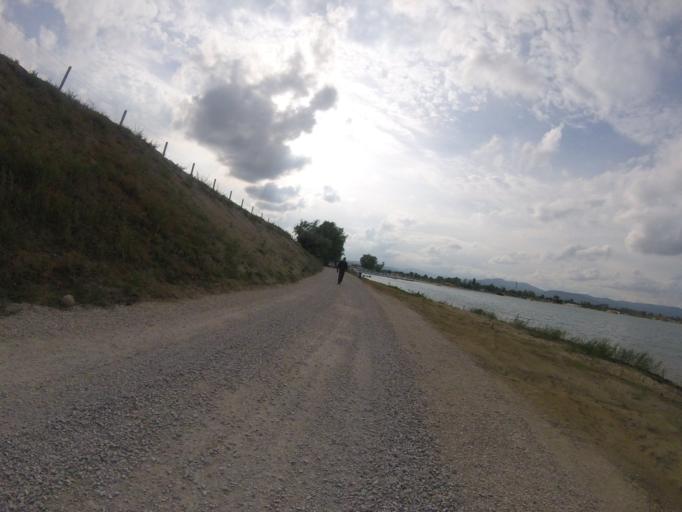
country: HU
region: Pest
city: Budakalasz
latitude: 47.6225
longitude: 19.0756
